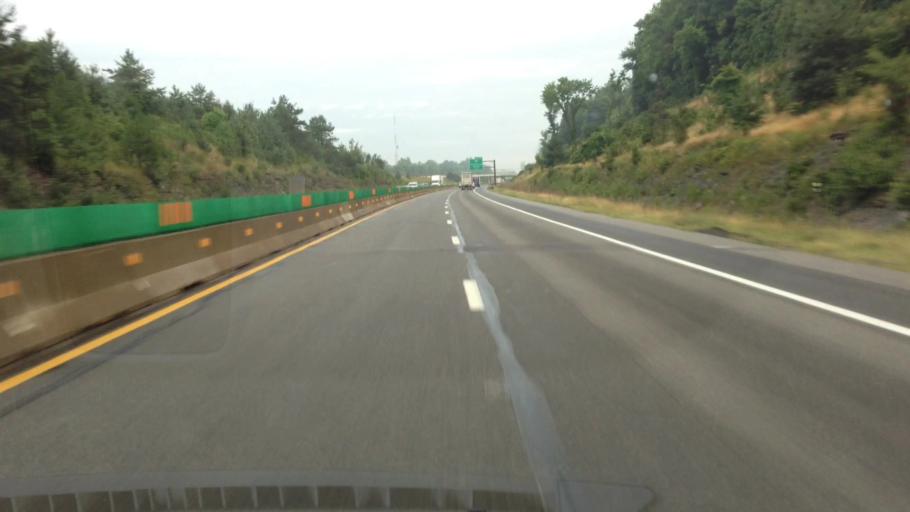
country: US
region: Ohio
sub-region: Summit County
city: Richfield
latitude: 41.2578
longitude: -81.6011
